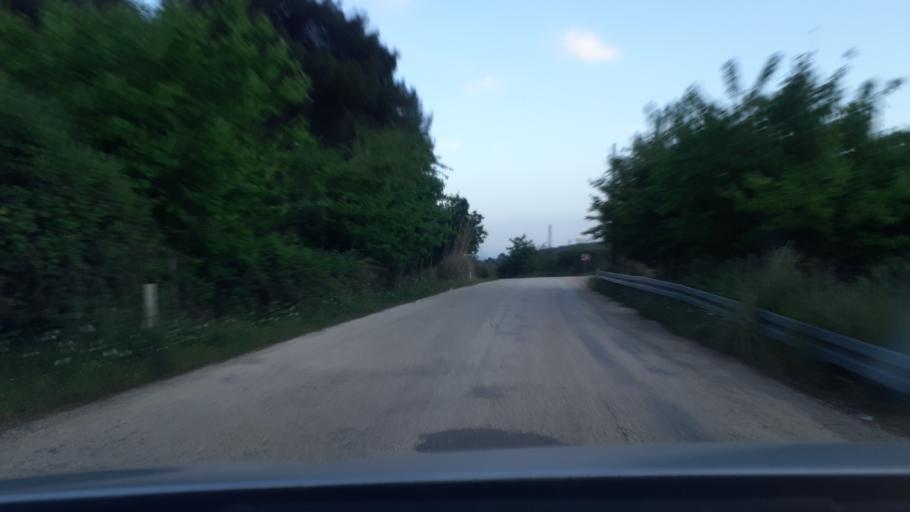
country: TR
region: Hatay
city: Kirikhan
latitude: 36.5198
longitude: 36.3182
